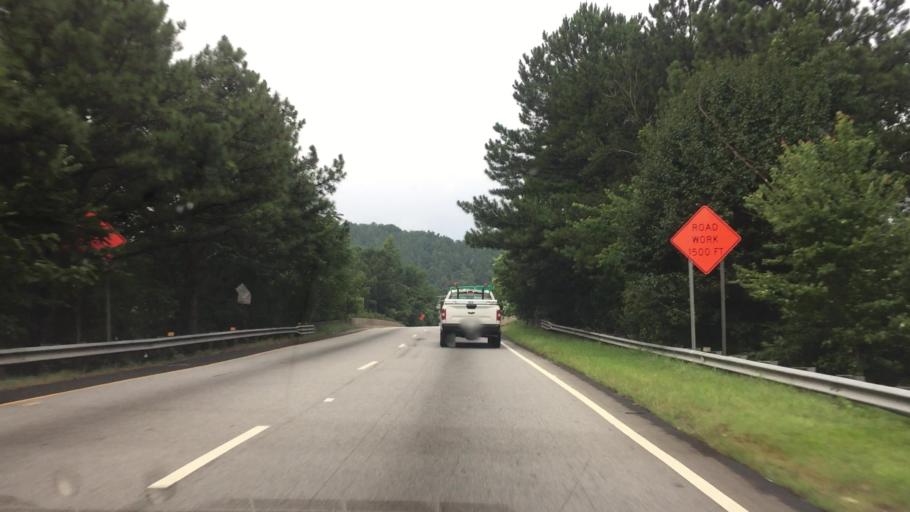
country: US
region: Georgia
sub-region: Clayton County
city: Conley
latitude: 33.6722
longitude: -84.3333
